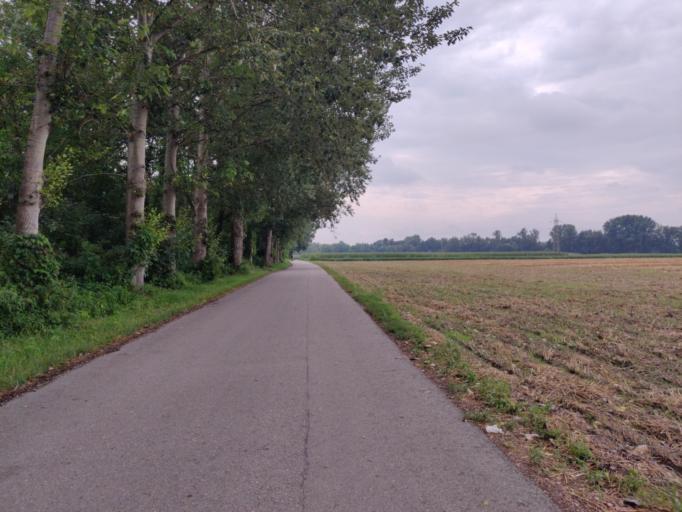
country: AT
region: Upper Austria
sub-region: Politischer Bezirk Linz-Land
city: Enns
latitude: 48.2348
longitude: 14.4670
